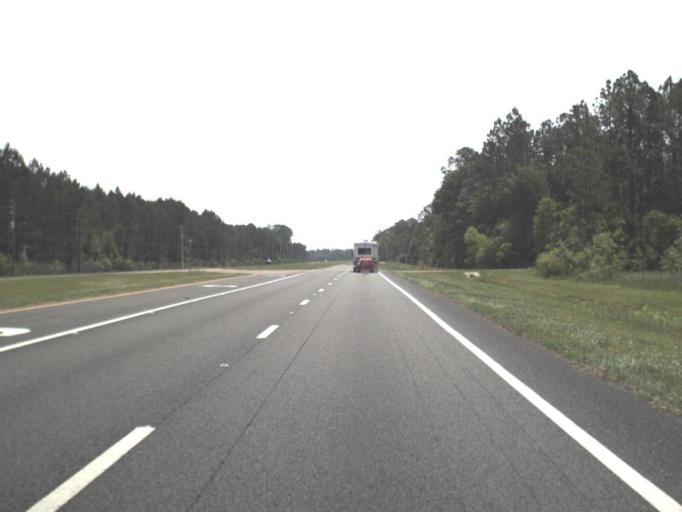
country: US
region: Florida
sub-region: Nassau County
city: Yulee
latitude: 30.6136
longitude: -81.6888
